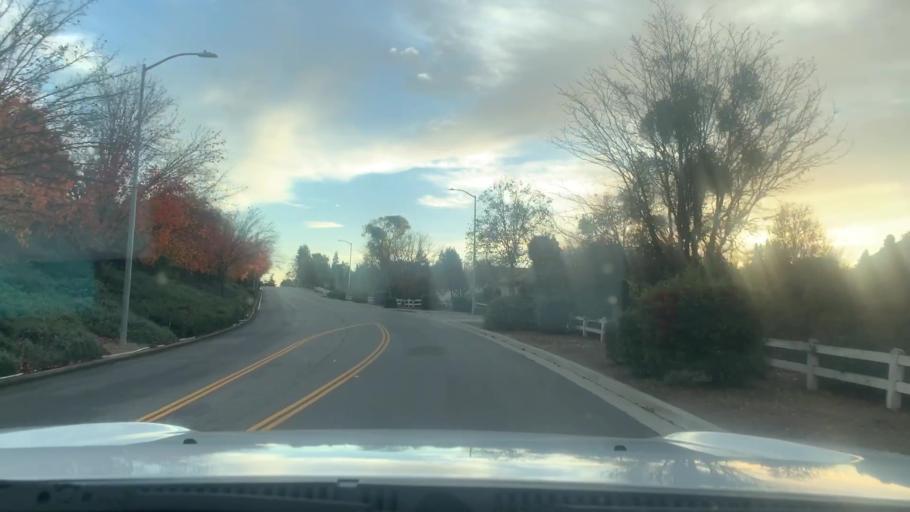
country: US
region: California
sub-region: San Luis Obispo County
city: Paso Robles
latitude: 35.6332
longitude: -120.6593
